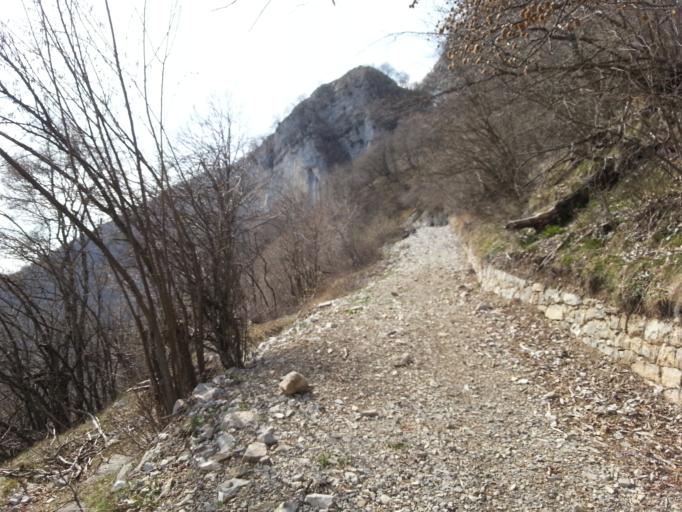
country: IT
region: Lombardy
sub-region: Provincia di Como
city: Mezzegra
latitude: 46.0020
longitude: 9.2047
